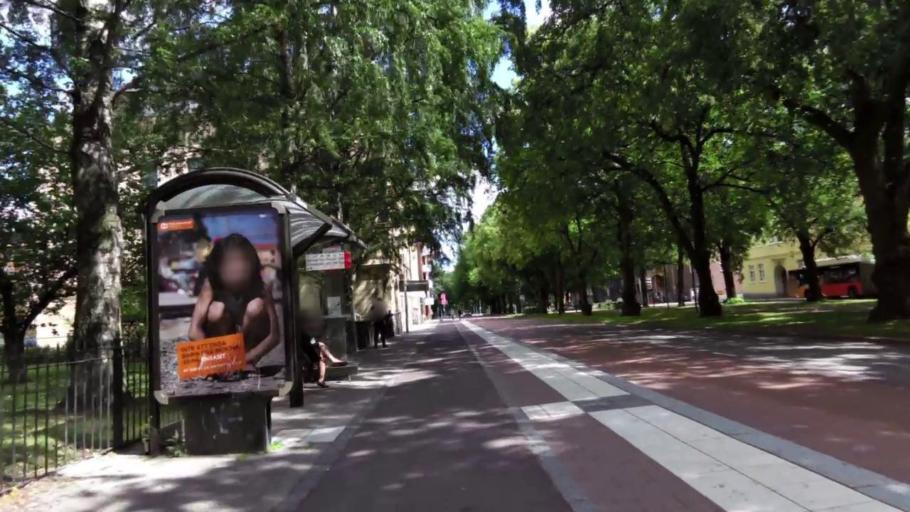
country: SE
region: OEstergoetland
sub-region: Linkopings Kommun
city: Linkoping
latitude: 58.4146
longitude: 15.6204
